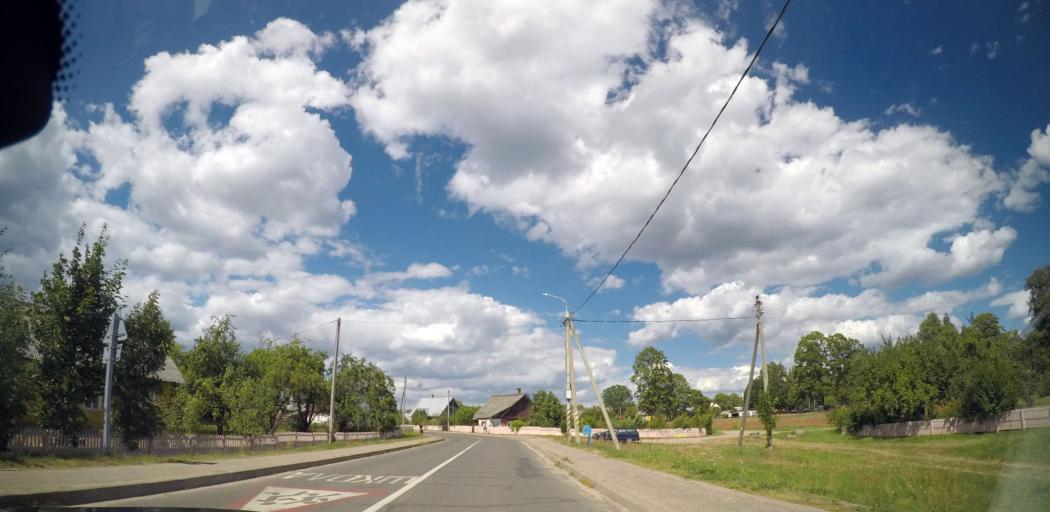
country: LT
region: Alytaus apskritis
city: Druskininkai
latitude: 53.8821
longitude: 24.1393
